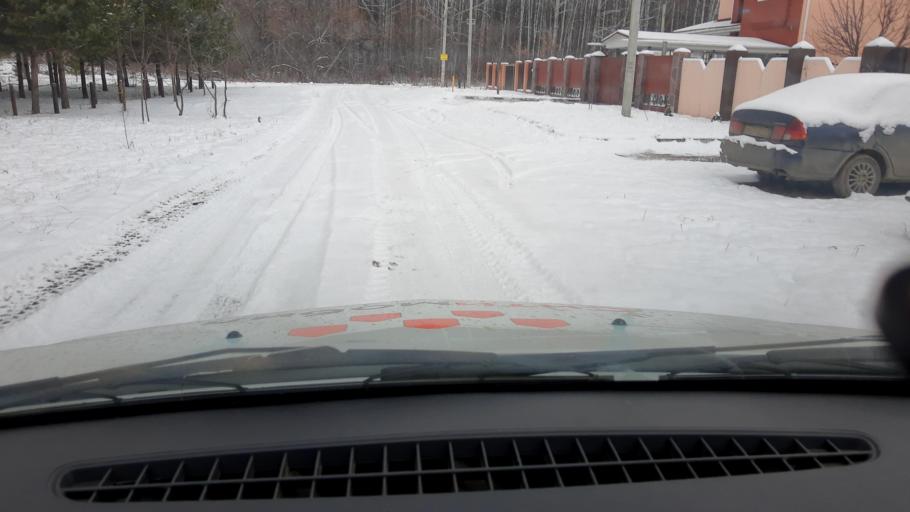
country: RU
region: Bashkortostan
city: Ufa
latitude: 54.7885
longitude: 56.1603
